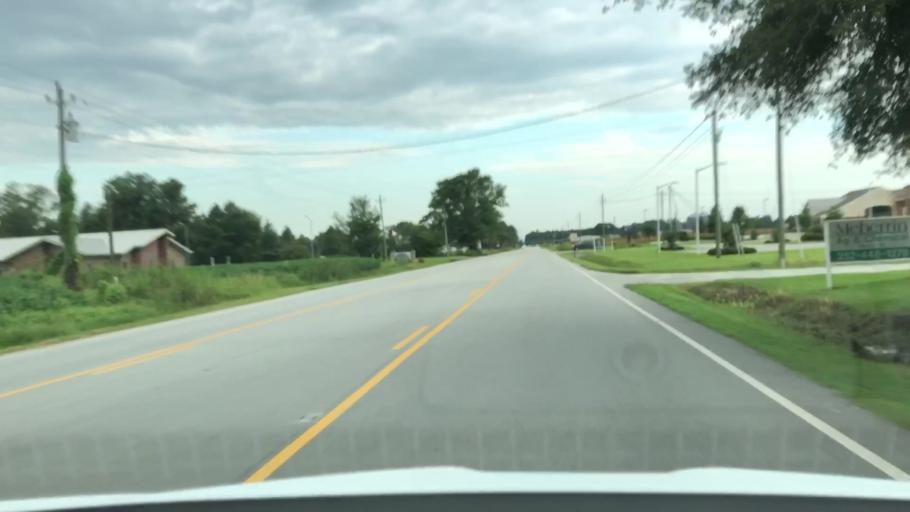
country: US
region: North Carolina
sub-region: Jones County
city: Trenton
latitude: 35.0677
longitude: -77.3655
